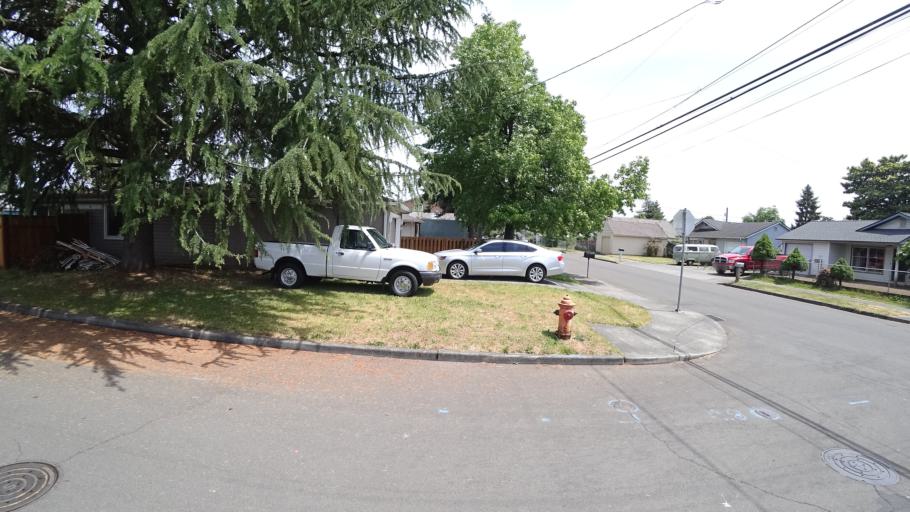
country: US
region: Oregon
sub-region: Multnomah County
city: Lents
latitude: 45.4643
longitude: -122.5966
